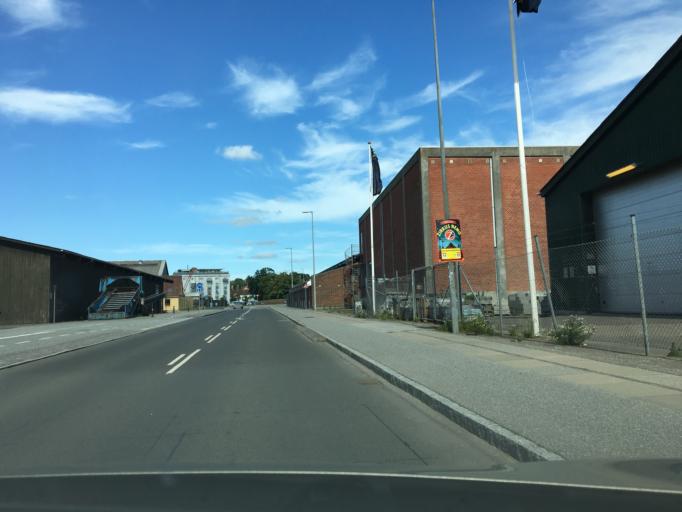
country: DK
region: South Denmark
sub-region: Svendborg Kommune
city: Svendborg
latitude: 55.0619
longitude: 10.6198
